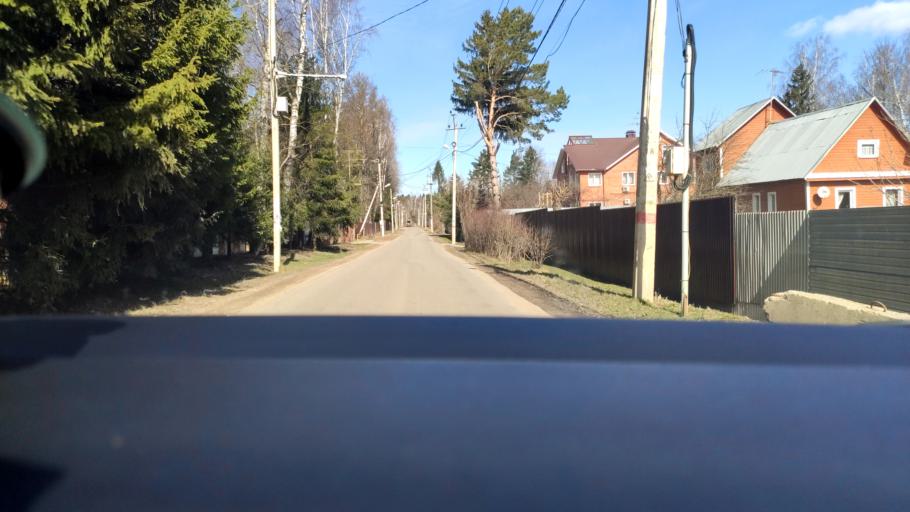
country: RU
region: Moskovskaya
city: Aprelevka
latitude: 55.5332
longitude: 37.0519
